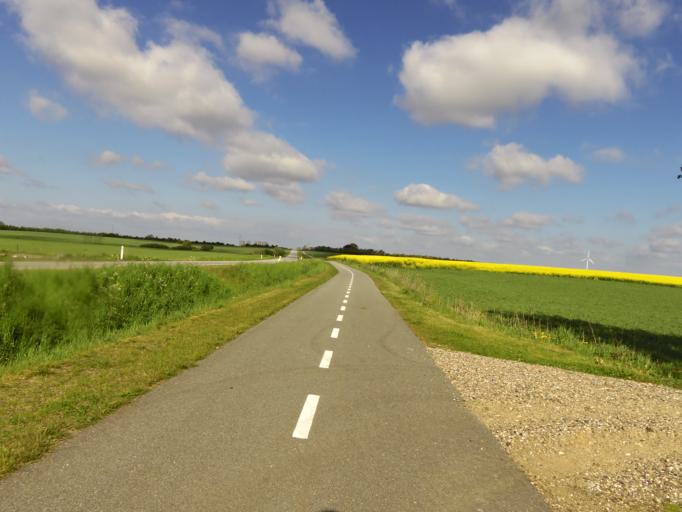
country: DK
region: South Denmark
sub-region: Vejen Kommune
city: Rodding
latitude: 55.3546
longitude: 8.9898
